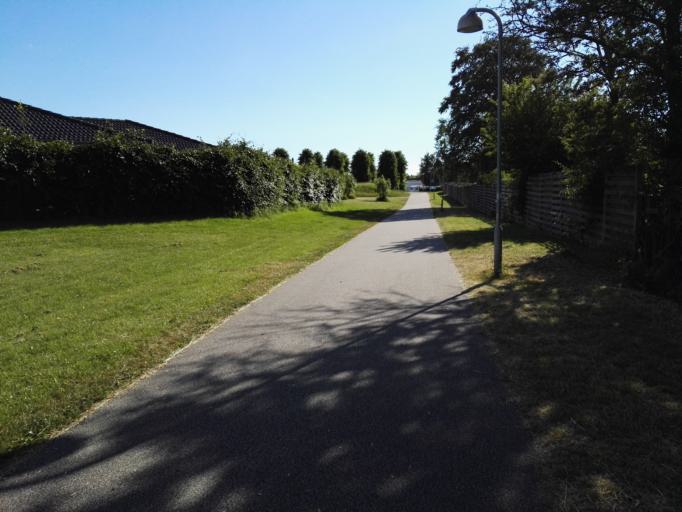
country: DK
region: Capital Region
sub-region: Egedal Kommune
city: Olstykke
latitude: 55.7883
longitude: 12.1465
